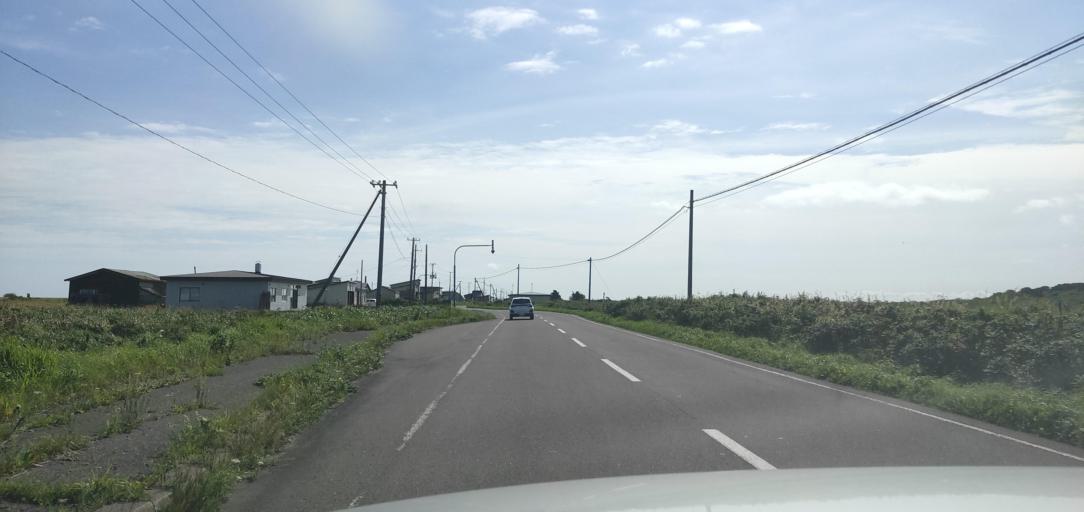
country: JP
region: Hokkaido
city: Shibetsu
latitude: 43.6327
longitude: 145.1827
